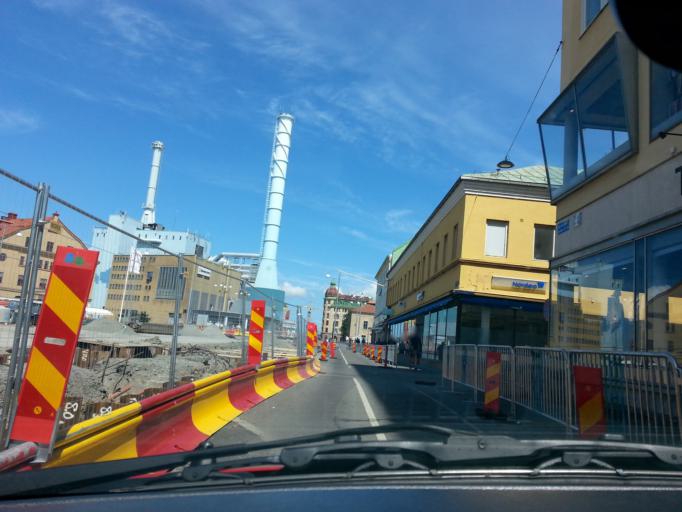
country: SE
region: Vaestra Goetaland
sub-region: Goteborg
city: Goeteborg
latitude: 57.7008
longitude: 11.9543
